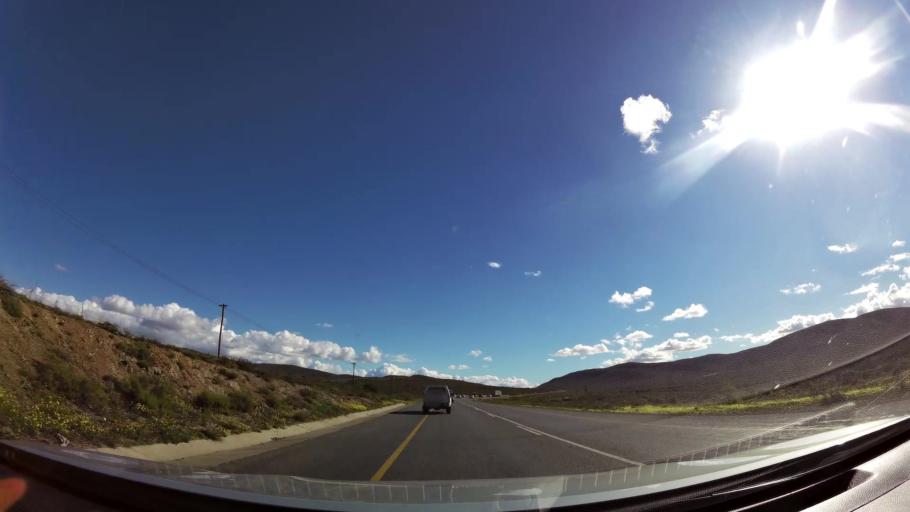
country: ZA
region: Western Cape
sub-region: Cape Winelands District Municipality
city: Worcester
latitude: -33.7377
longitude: 19.6830
